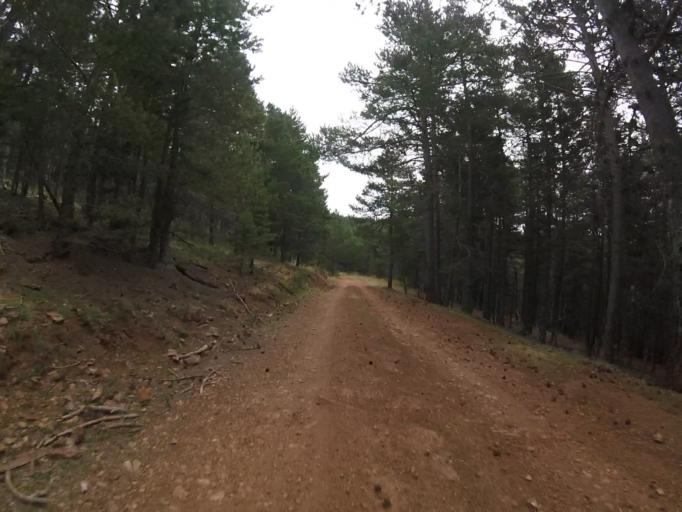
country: ES
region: Aragon
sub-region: Provincia de Teruel
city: Valdelinares
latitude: 40.3580
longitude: -0.6033
